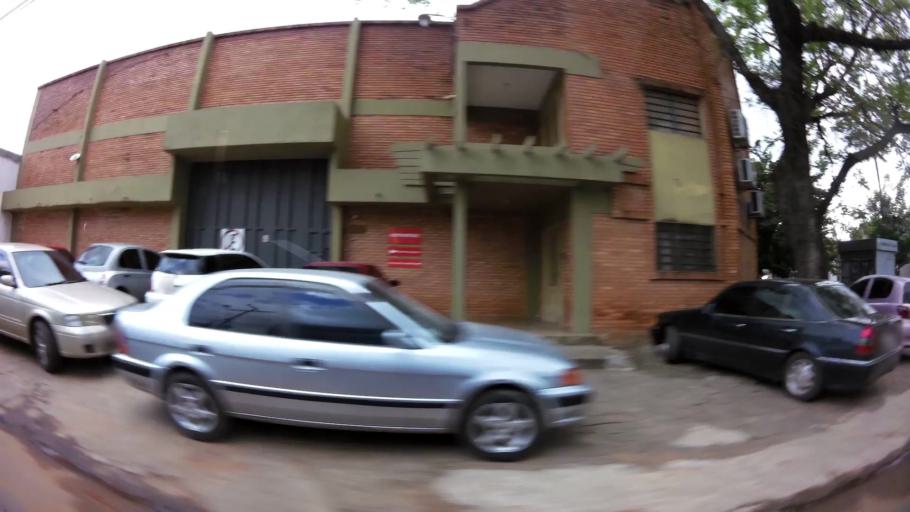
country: PY
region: Central
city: Fernando de la Mora
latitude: -25.3325
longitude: -57.5532
